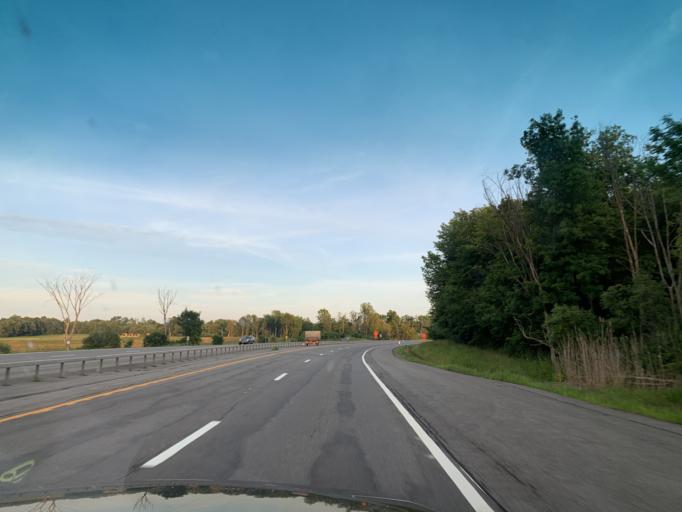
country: US
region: New York
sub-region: Oneida County
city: Chadwicks
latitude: 43.0314
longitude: -75.2680
